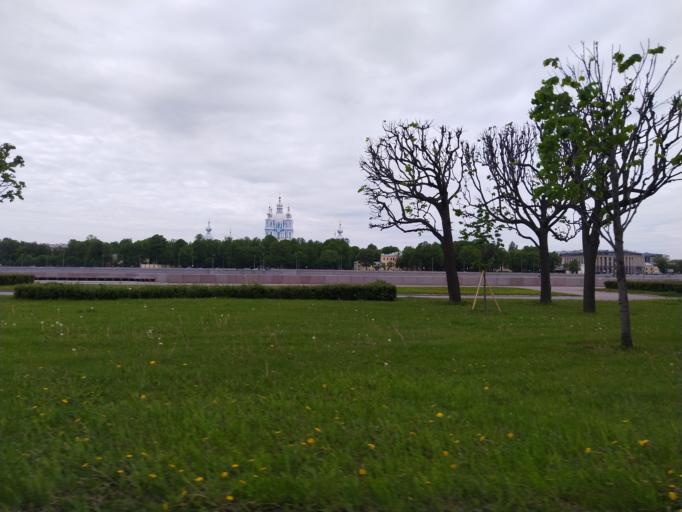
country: RU
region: Leningrad
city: Finlyandskiy
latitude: 59.9491
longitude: 30.4069
